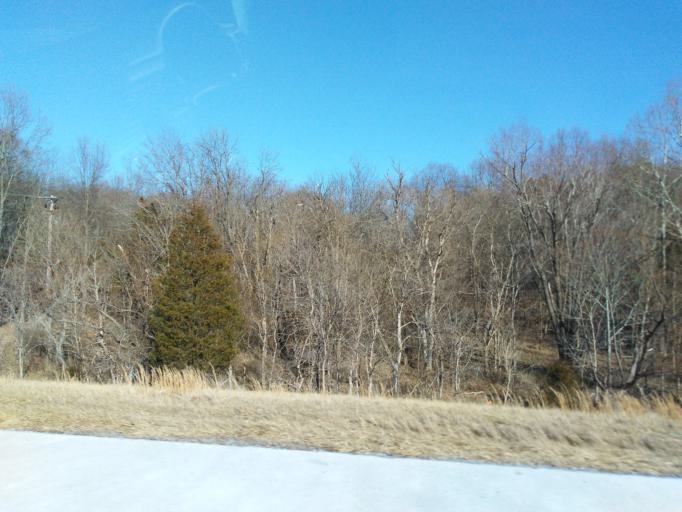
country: US
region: Illinois
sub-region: Johnson County
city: Vienna
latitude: 37.4202
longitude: -88.8727
